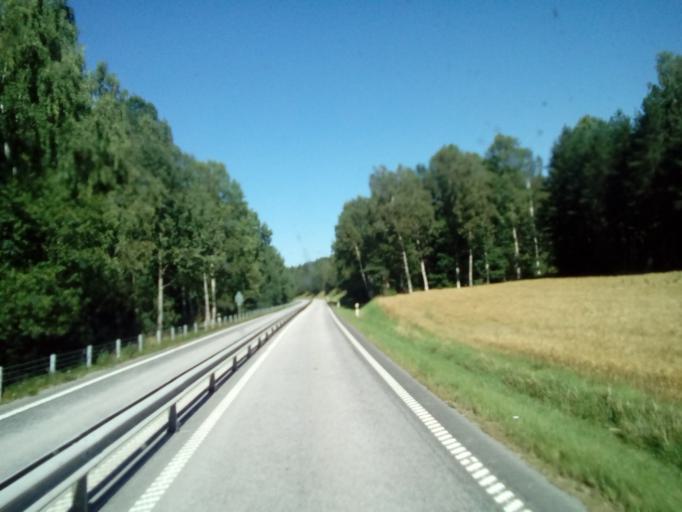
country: SE
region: OEstergoetland
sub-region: Kinda Kommun
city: Kisa
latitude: 58.0316
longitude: 15.6590
